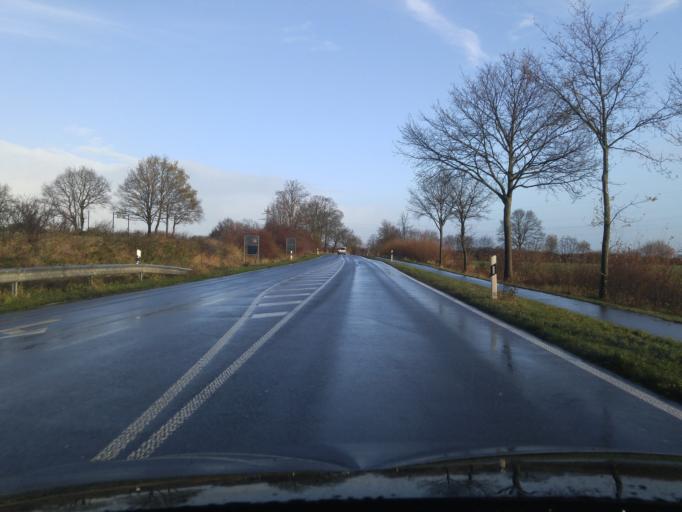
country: DE
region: Schleswig-Holstein
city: Ratekau
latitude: 53.9520
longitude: 10.7518
